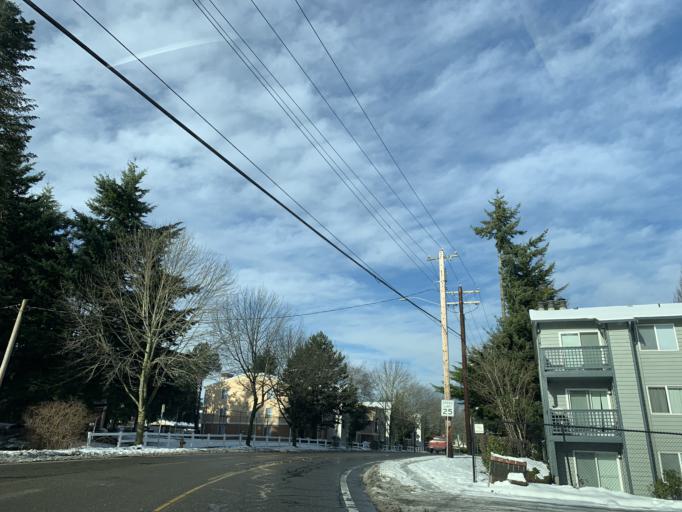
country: US
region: Washington
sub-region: Snohomish County
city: Martha Lake
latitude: 47.9181
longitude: -122.2402
